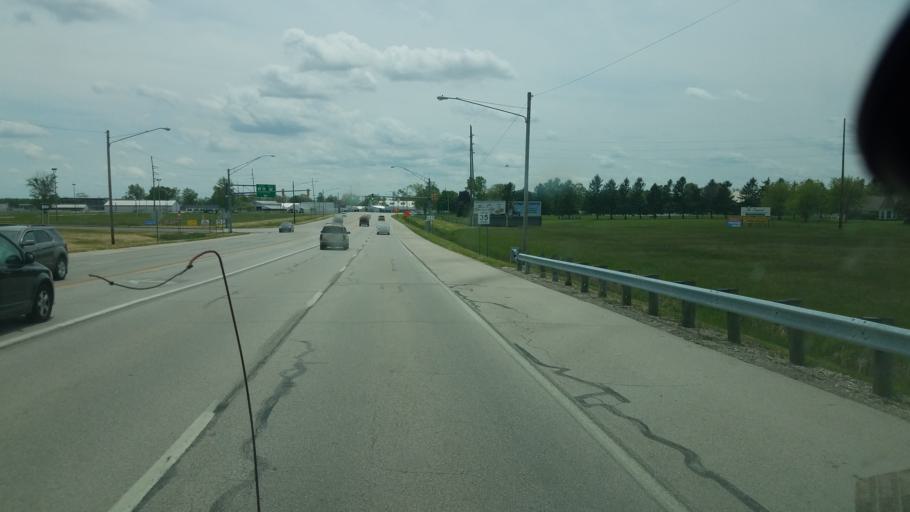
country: US
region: Ohio
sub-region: Sandusky County
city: Fremont
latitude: 41.3660
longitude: -83.1172
